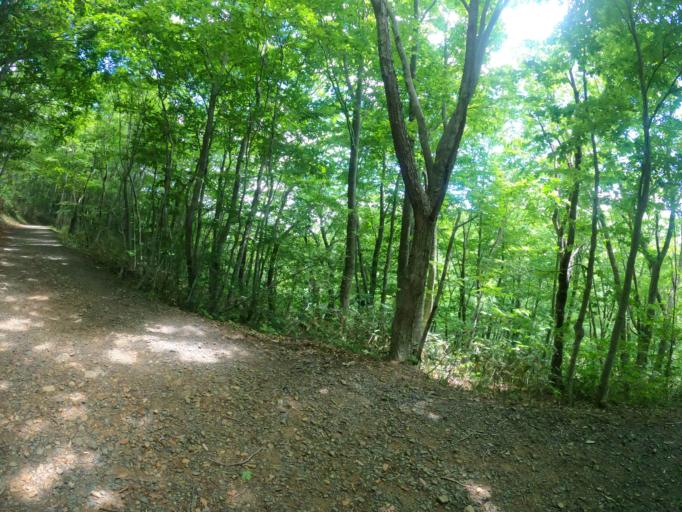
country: JP
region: Iwate
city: Ichinoseki
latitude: 38.9106
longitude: 140.8116
